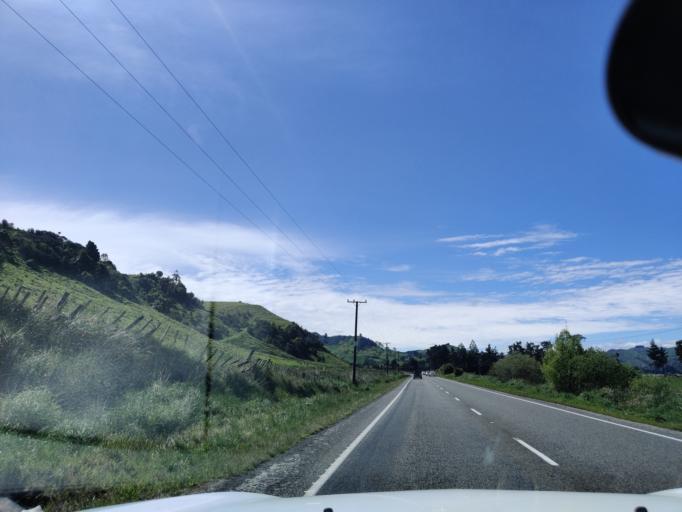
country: NZ
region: Manawatu-Wanganui
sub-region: Ruapehu District
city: Waiouru
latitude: -39.8493
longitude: 175.7349
